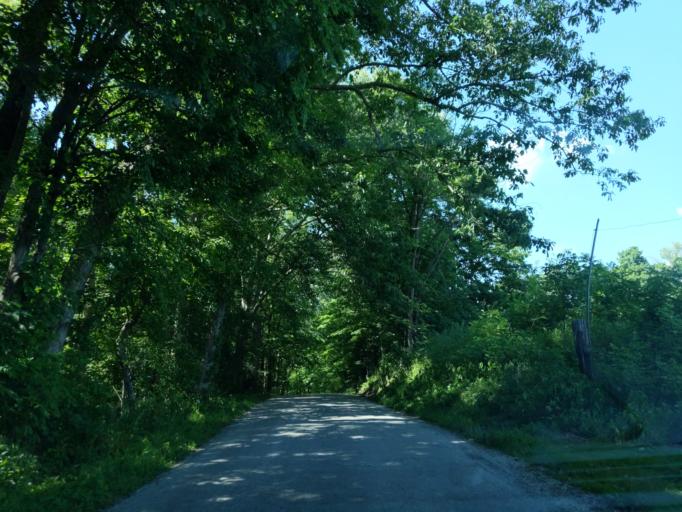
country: US
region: Indiana
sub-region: Ripley County
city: Osgood
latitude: 39.1993
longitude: -85.4165
